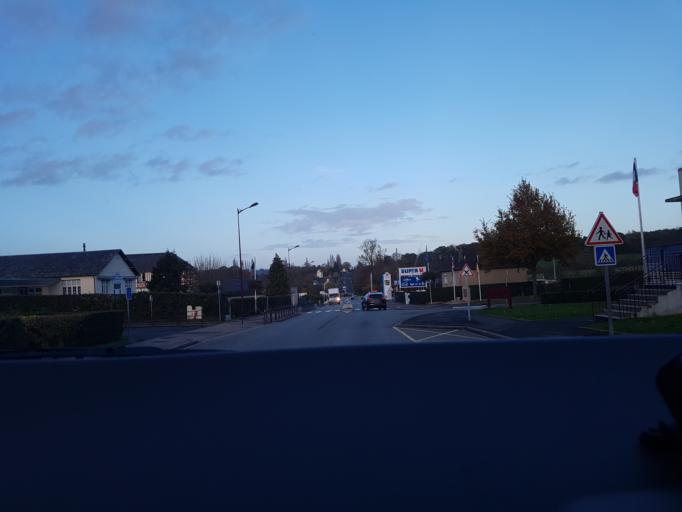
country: FR
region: Lower Normandy
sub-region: Departement du Calvados
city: Dozule
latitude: 49.2325
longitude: -0.0405
